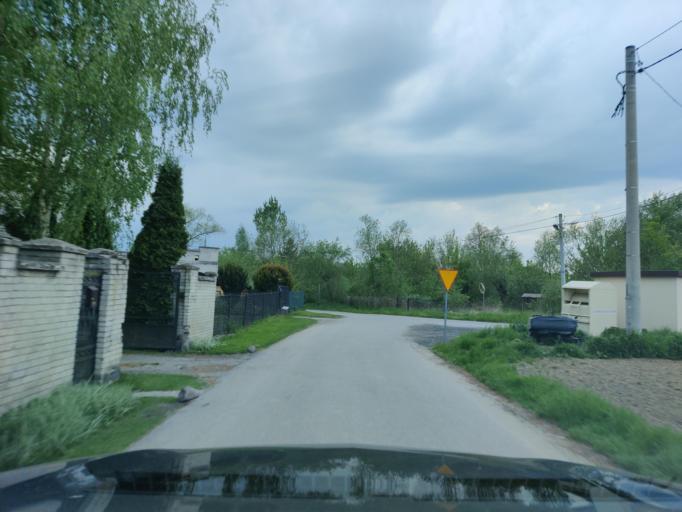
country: PL
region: Masovian Voivodeship
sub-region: Powiat piaseczynski
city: Konstancin-Jeziorna
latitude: 52.1206
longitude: 21.1659
